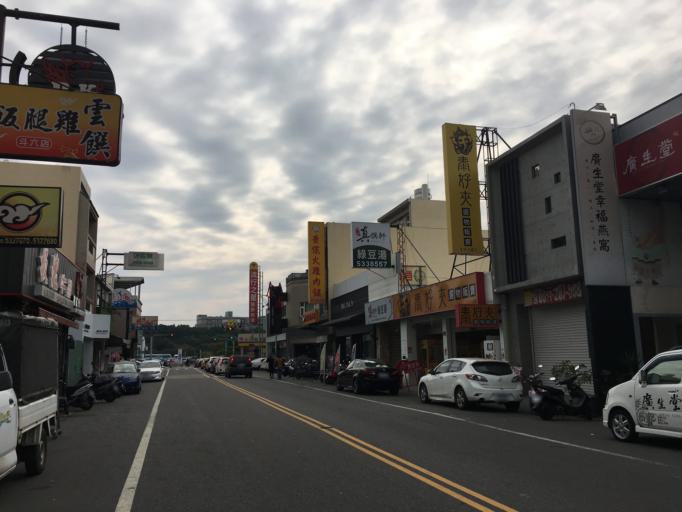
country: TW
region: Taiwan
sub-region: Yunlin
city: Douliu
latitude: 23.6994
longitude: 120.5371
